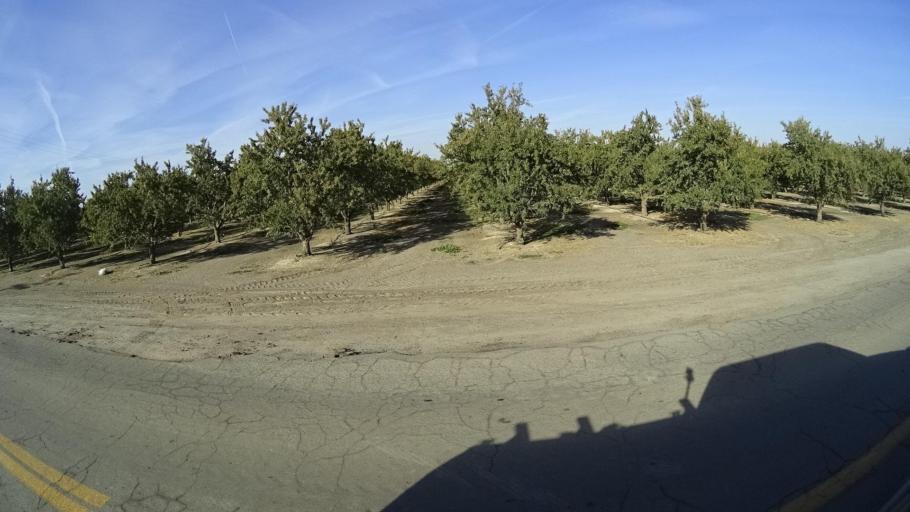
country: US
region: California
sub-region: Kern County
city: McFarland
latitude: 35.7034
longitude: -119.2346
